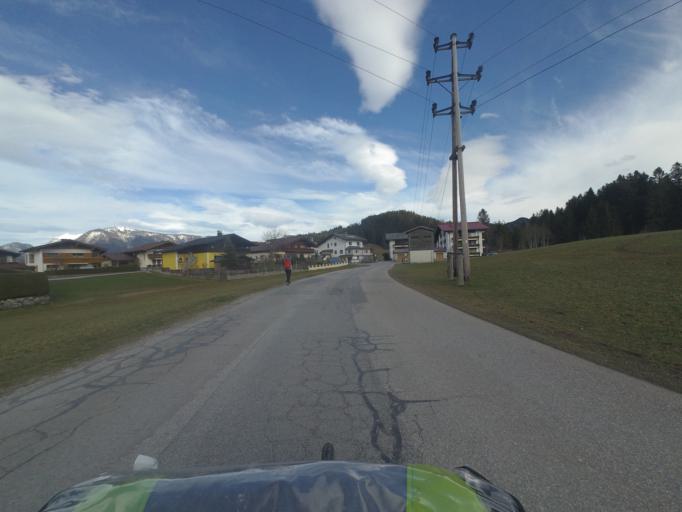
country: AT
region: Salzburg
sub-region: Politischer Bezirk Hallein
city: Abtenau
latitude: 47.5740
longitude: 13.3454
